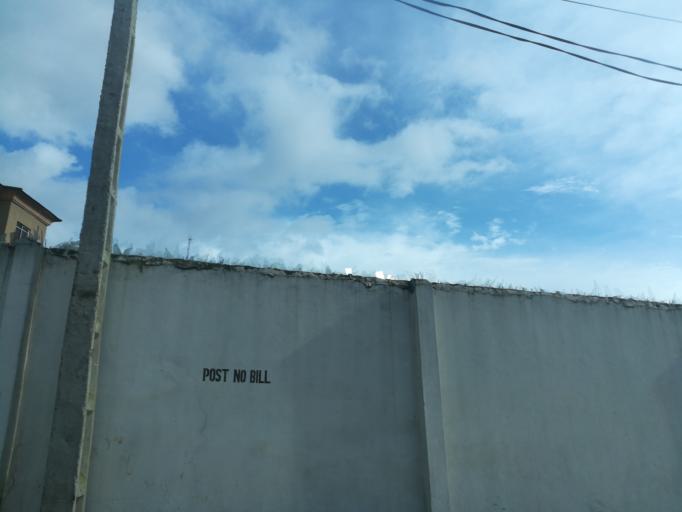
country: NG
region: Lagos
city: Ikeja
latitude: 6.6205
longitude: 3.3533
